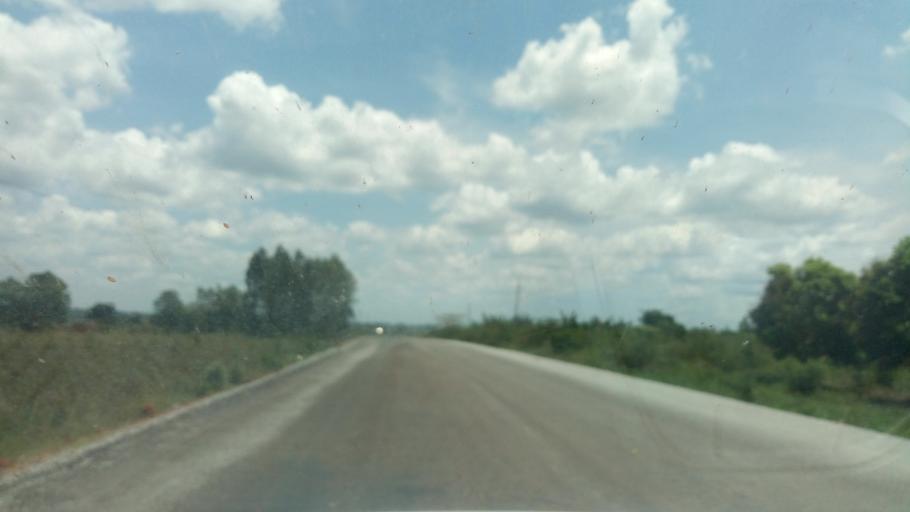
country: UG
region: Western Region
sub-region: Kiryandongo District
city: Kiryandongo
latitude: 1.7901
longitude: 31.9462
